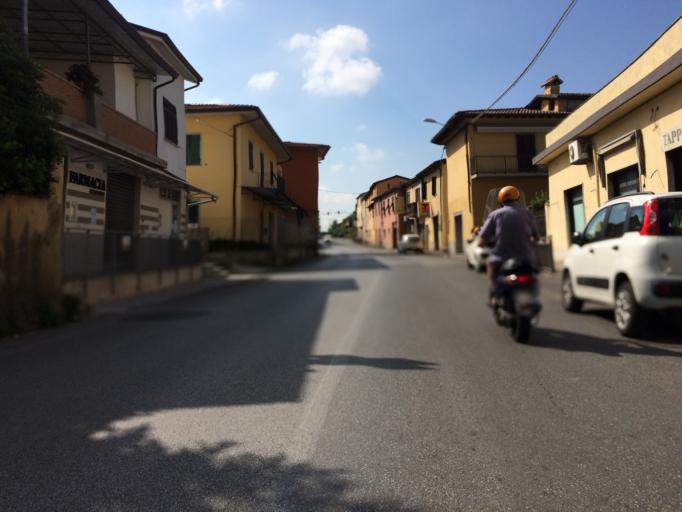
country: IT
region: Tuscany
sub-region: Provincia di Massa-Carrara
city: San Vito-Cerreto
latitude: 44.0230
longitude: 10.1472
